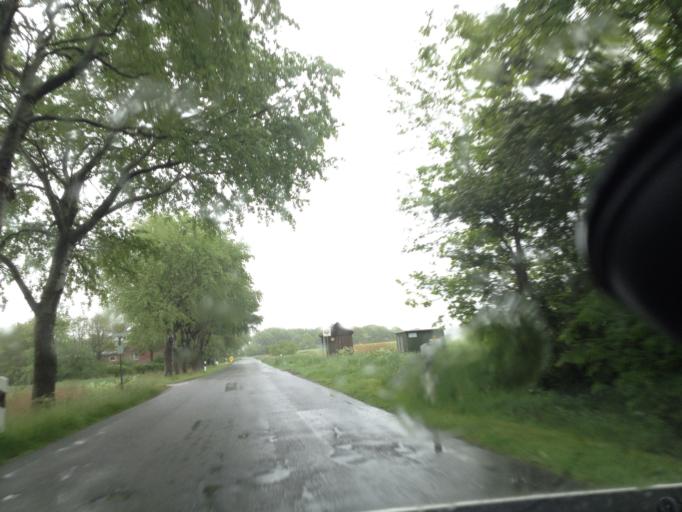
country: DE
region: Schleswig-Holstein
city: Rodenas
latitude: 54.8877
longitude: 8.7075
